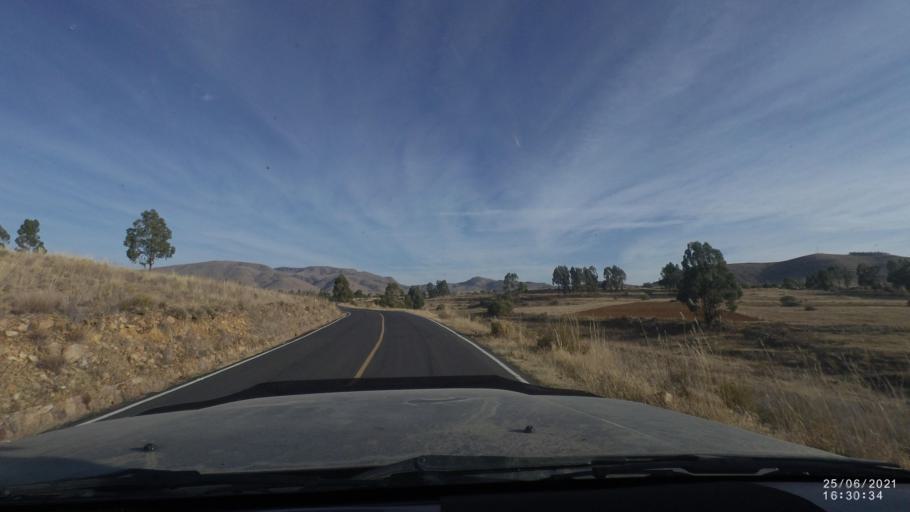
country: BO
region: Cochabamba
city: Arani
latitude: -17.7938
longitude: -65.8042
